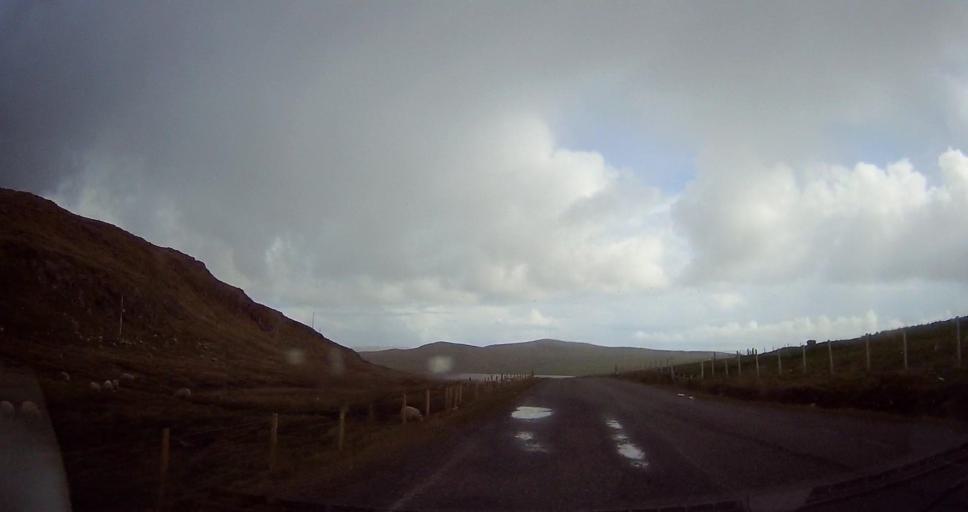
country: GB
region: Scotland
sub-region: Shetland Islands
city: Lerwick
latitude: 60.5431
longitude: -1.3440
